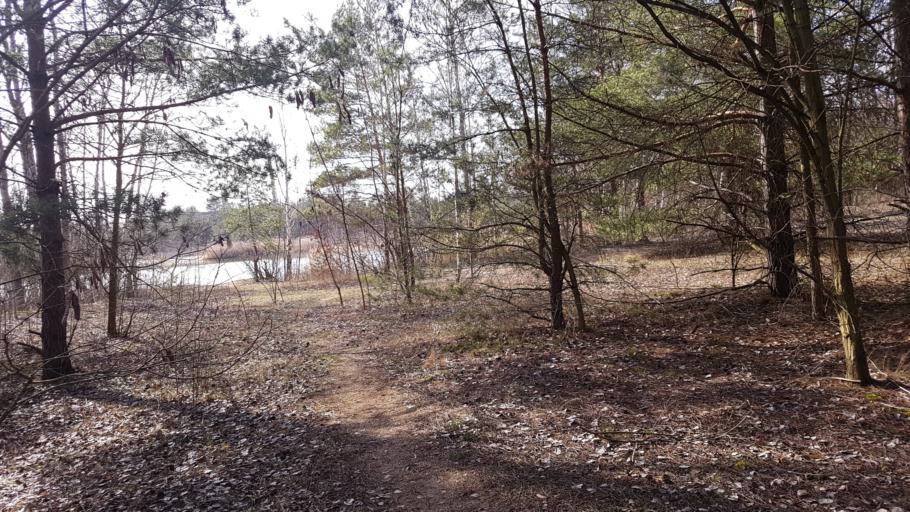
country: DE
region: Brandenburg
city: Doberlug-Kirchhain
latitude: 51.6266
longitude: 13.5723
